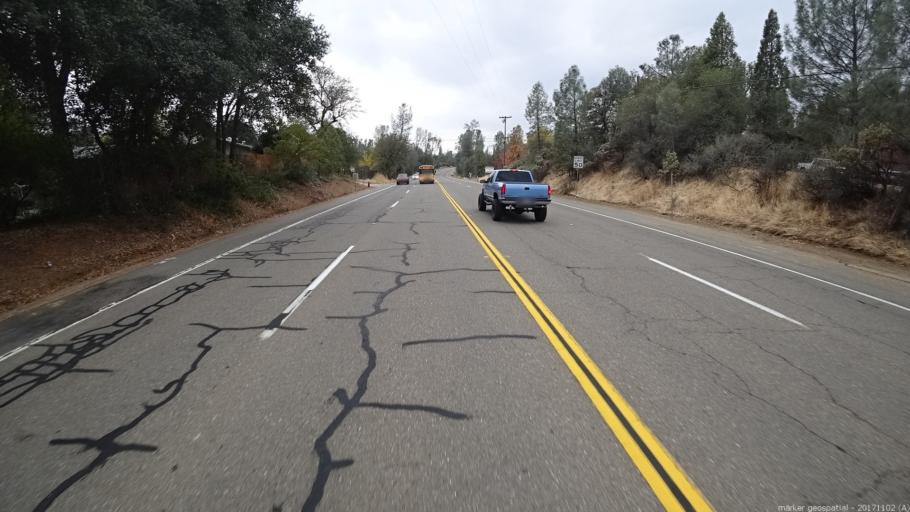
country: US
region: California
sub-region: Shasta County
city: Central Valley (historical)
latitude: 40.6522
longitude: -122.3968
